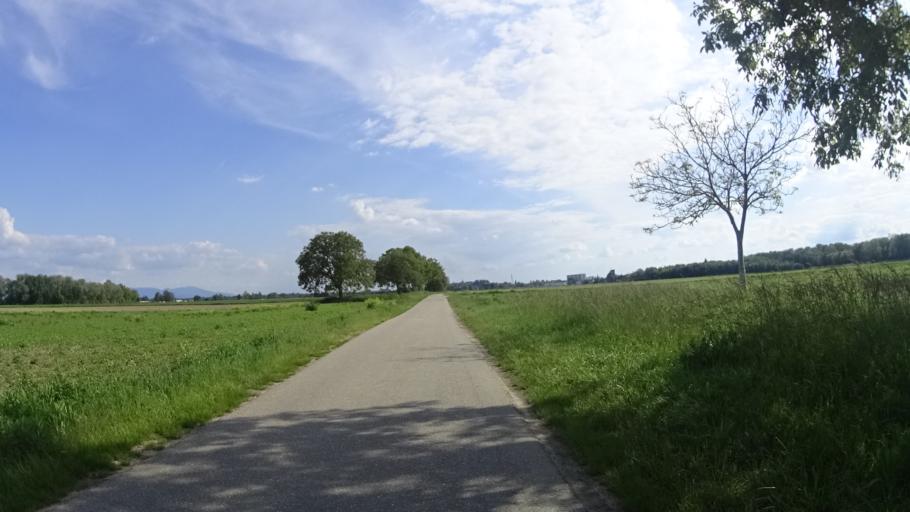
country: DE
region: Baden-Wuerttemberg
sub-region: Freiburg Region
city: Breisach am Rhein
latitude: 48.0573
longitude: 7.5877
